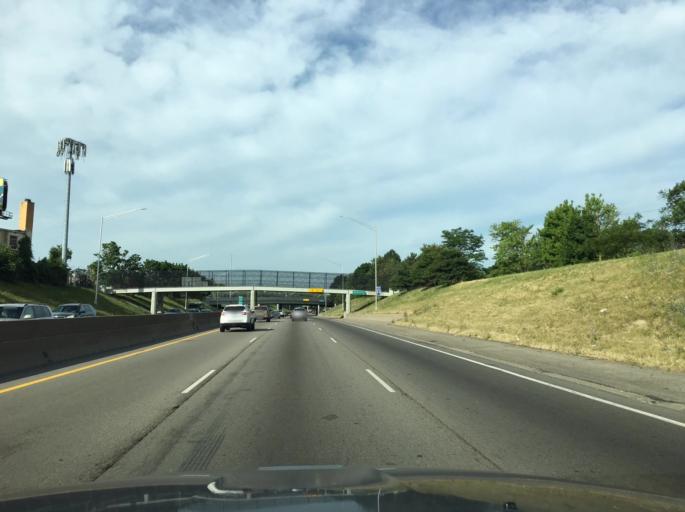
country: US
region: Michigan
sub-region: Wayne County
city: Harper Woods
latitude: 42.4108
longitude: -82.9462
